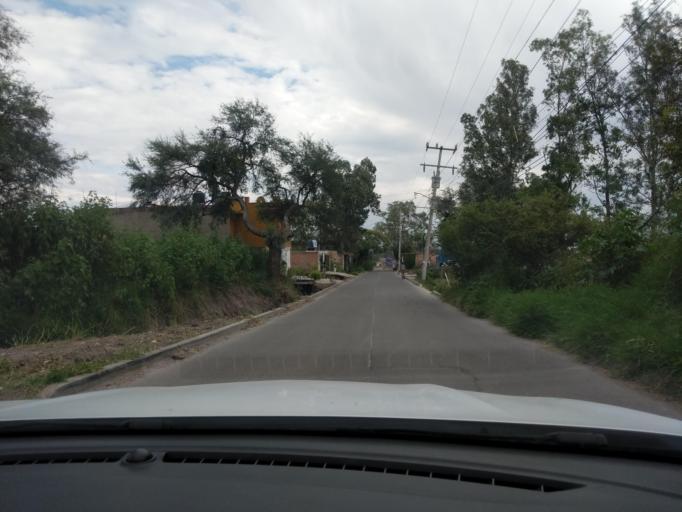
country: MX
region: Jalisco
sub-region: El Salto
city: Galaxia Bonito Jalisco
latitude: 20.5116
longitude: -103.1905
